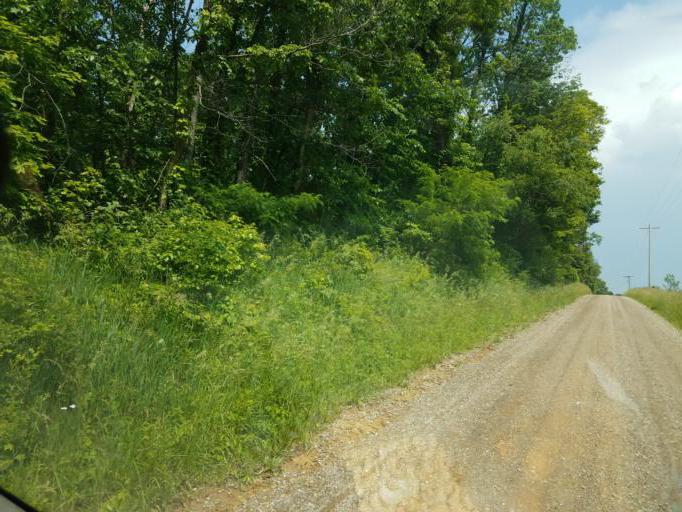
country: US
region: Ohio
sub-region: Knox County
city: Oak Hill
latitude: 40.3566
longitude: -82.2695
